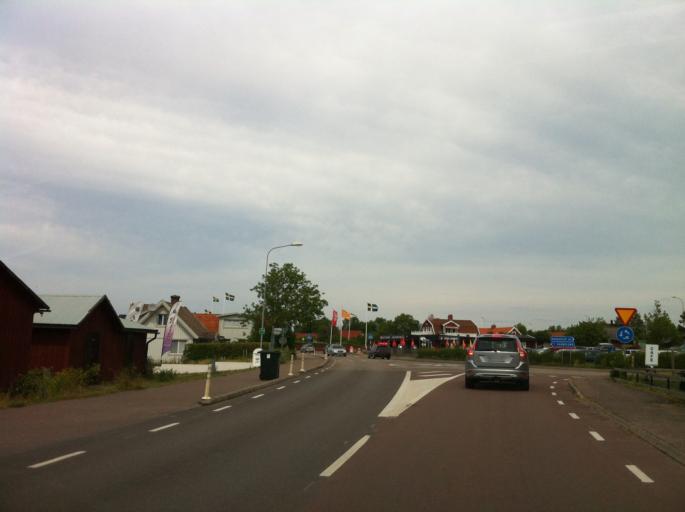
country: SE
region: Kalmar
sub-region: Oskarshamns Kommun
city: Oskarshamn
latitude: 57.3241
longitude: 17.0074
